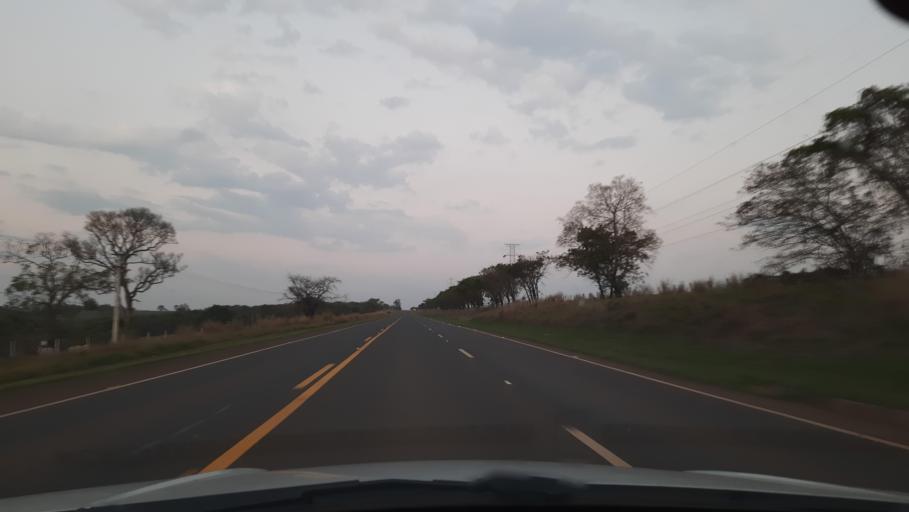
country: BR
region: Sao Paulo
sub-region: Casa Branca
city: Casa Branca
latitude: -21.8017
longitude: -47.1189
